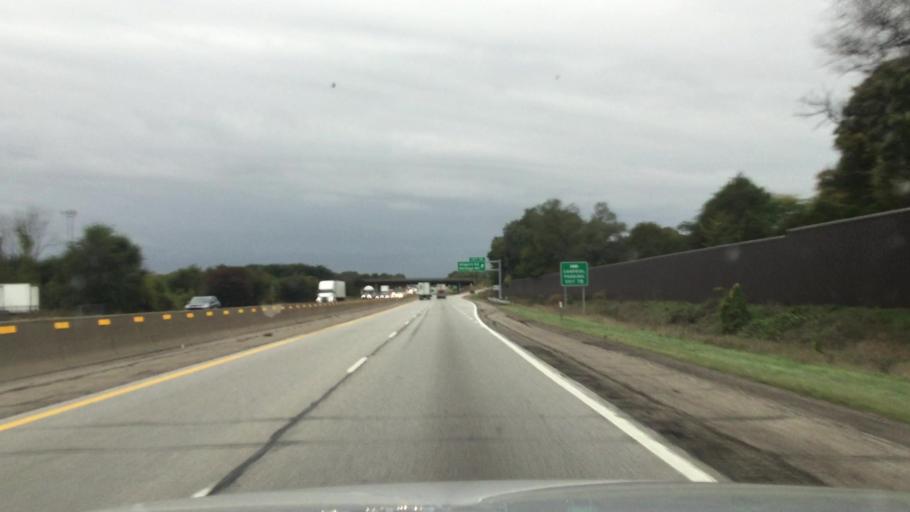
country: US
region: Michigan
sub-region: Kalamazoo County
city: Eastwood
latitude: 42.2486
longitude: -85.5506
